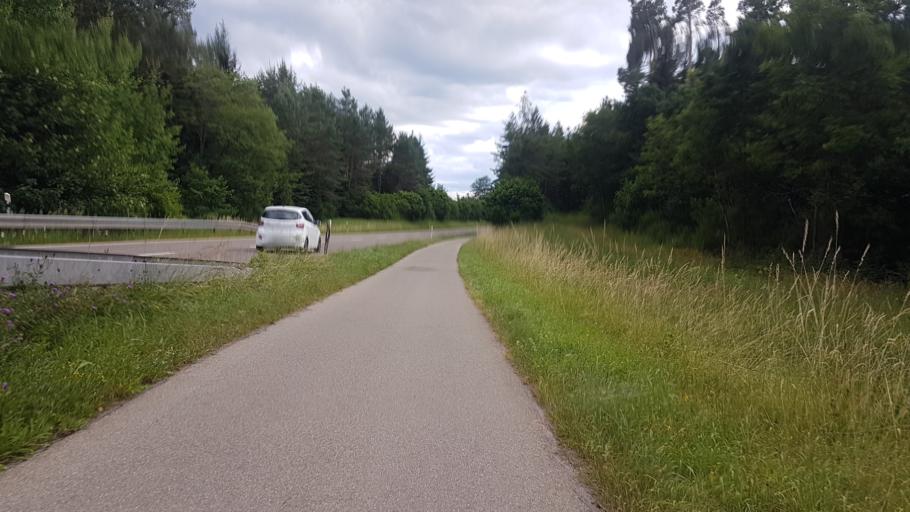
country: DE
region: Baden-Wuerttemberg
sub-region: Freiburg Region
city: Monchweiler
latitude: 48.0532
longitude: 8.4246
